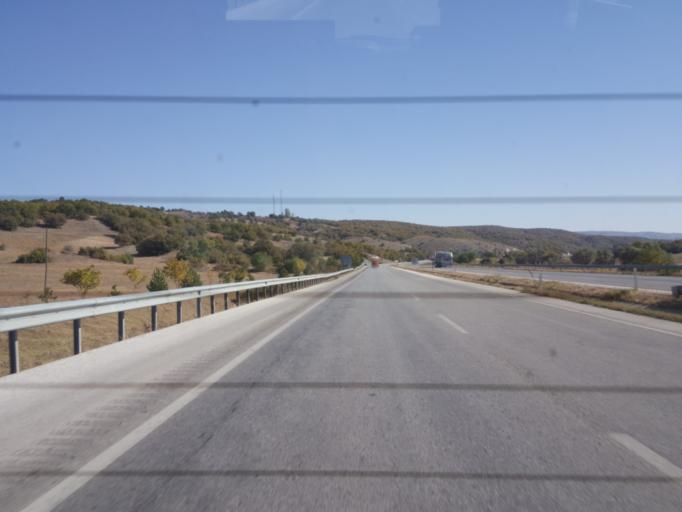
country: TR
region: Corum
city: Alaca
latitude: 40.3091
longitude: 34.6573
